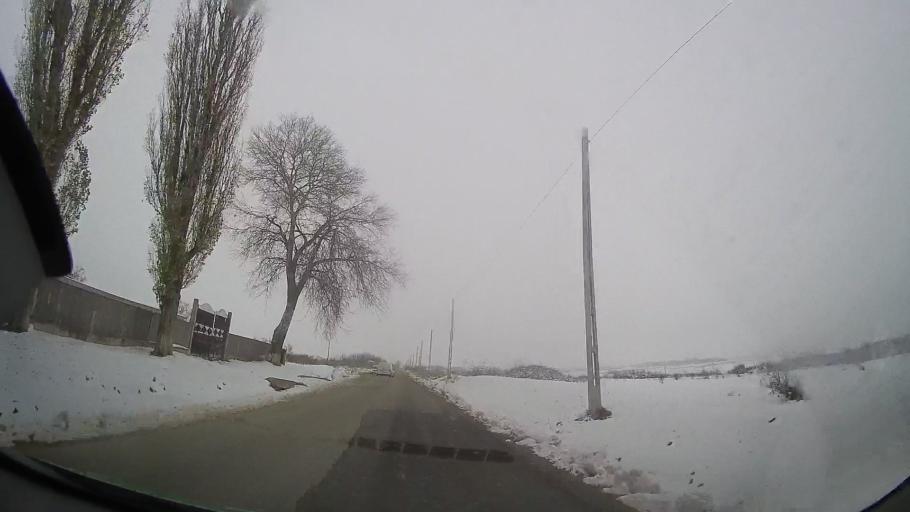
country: RO
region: Vaslui
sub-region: Comuna Todiresti
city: Todiresti
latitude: 46.8515
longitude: 27.3943
